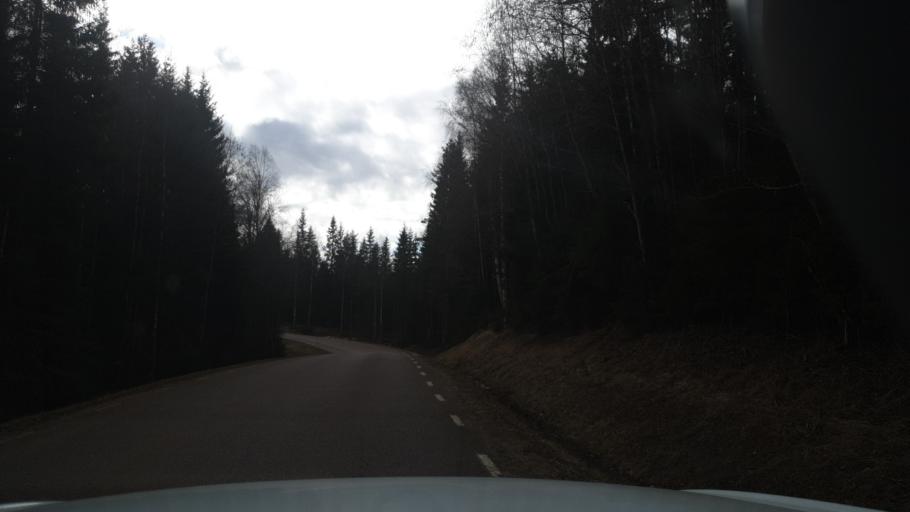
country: SE
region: Vaermland
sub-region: Arvika Kommun
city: Arvika
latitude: 59.8050
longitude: 12.8339
